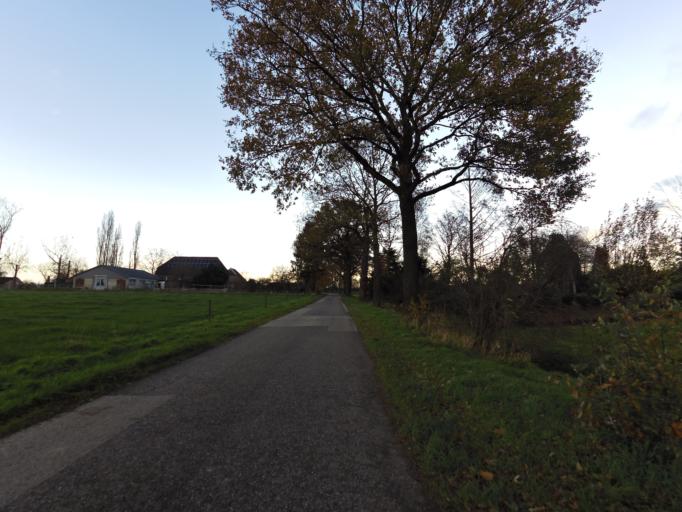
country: NL
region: Gelderland
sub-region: Oude IJsselstreek
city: Gendringen
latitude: 51.8406
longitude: 6.3841
